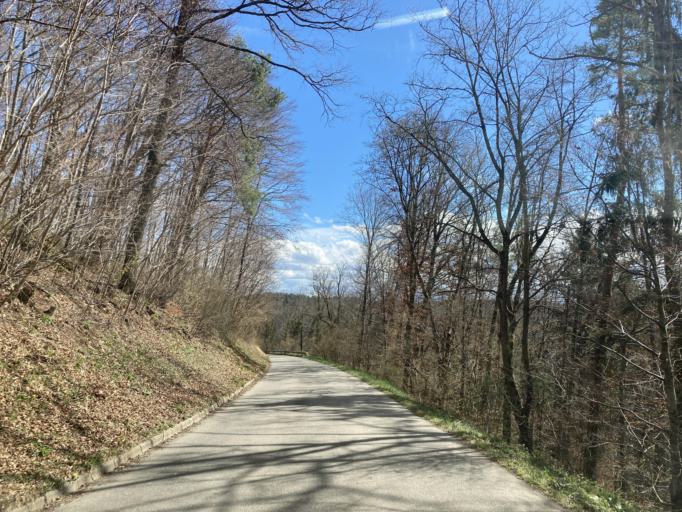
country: DE
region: Baden-Wuerttemberg
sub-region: Tuebingen Region
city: Hirrlingen
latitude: 48.4541
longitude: 8.8514
